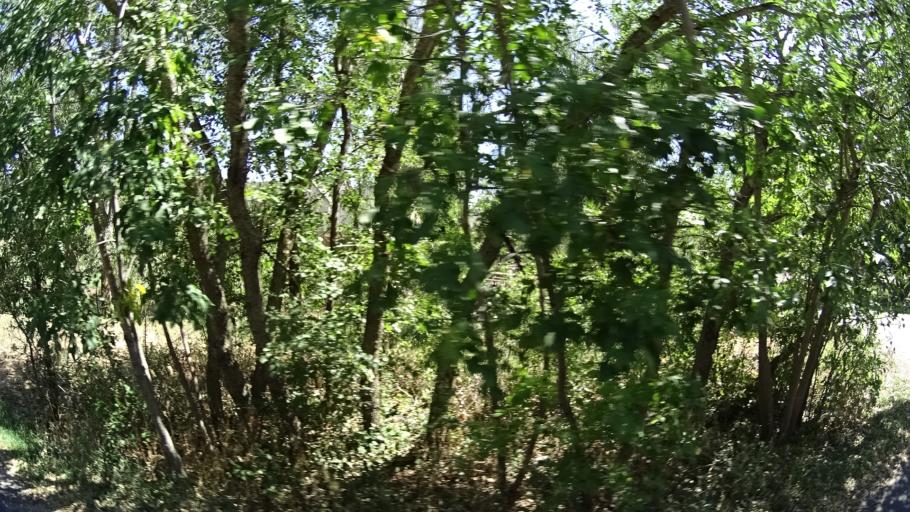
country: US
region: Colorado
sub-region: El Paso County
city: Colorado Springs
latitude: 38.7806
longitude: -104.8424
